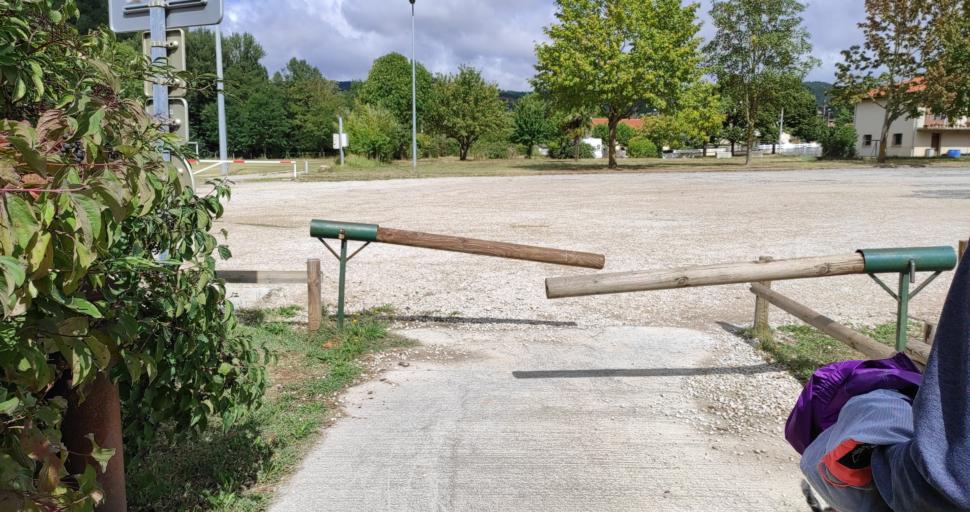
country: FR
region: Midi-Pyrenees
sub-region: Departement de l'Aveyron
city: Saint-Affrique
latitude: 43.9465
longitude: 2.8947
